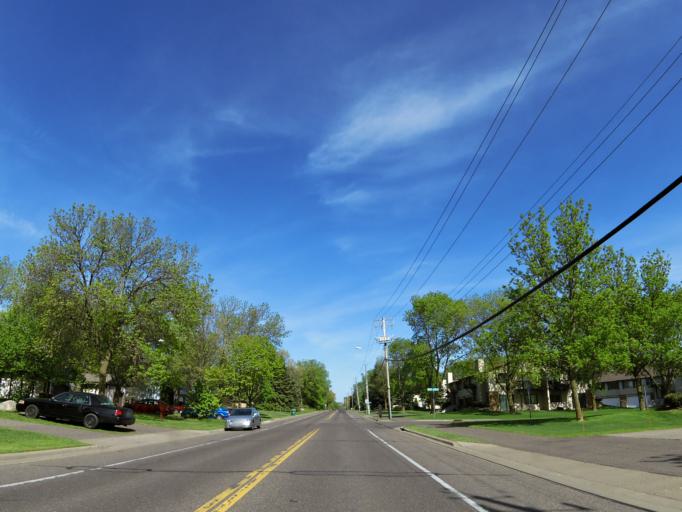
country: US
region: Minnesota
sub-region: Ramsey County
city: North Saint Paul
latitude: 45.0067
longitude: -92.9789
